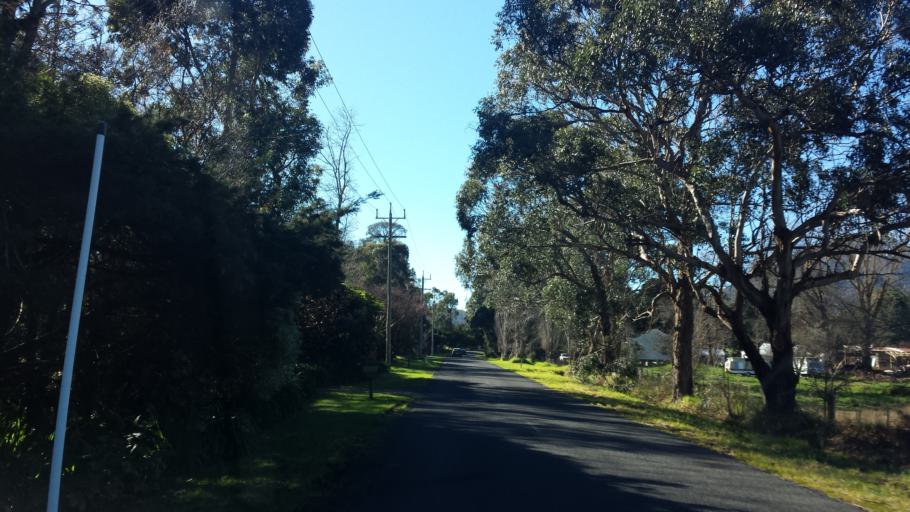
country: AU
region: Victoria
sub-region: Yarra Ranges
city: Healesville
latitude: -37.6698
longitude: 145.5259
